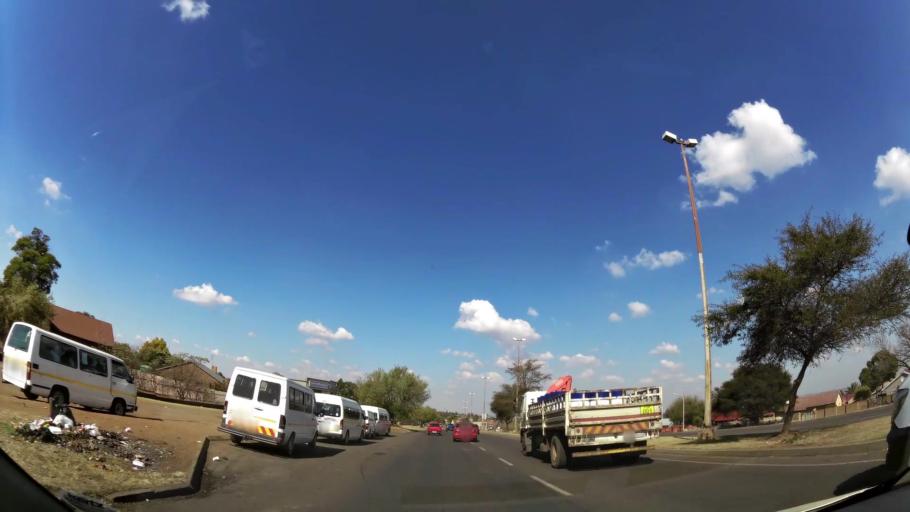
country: ZA
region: Mpumalanga
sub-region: Nkangala District Municipality
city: Witbank
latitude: -25.9033
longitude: 29.2354
